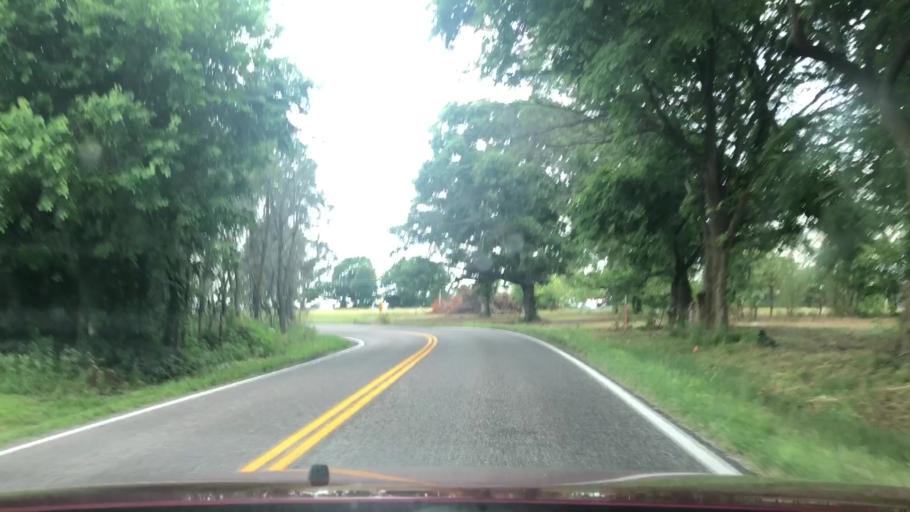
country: US
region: Missouri
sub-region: Christian County
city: Ozark
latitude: 36.9437
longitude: -93.2377
